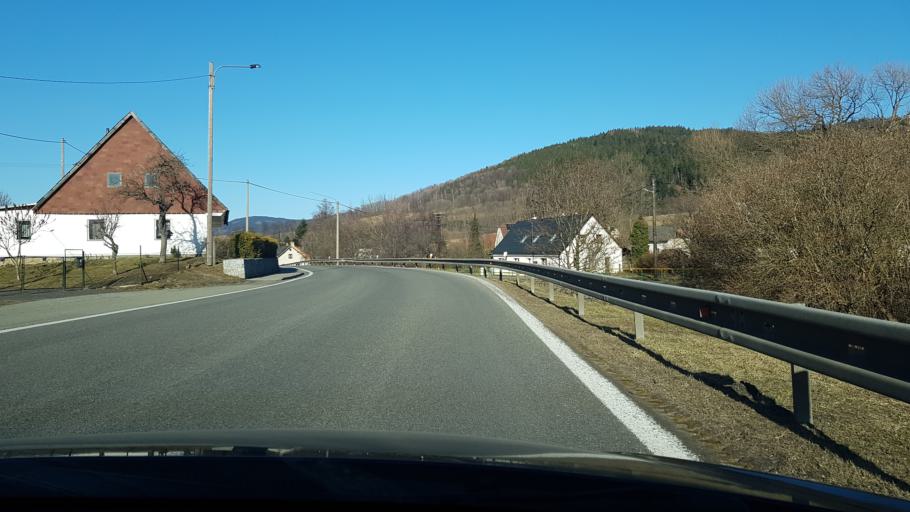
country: CZ
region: Olomoucky
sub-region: Okres Jesenik
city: Jesenik
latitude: 50.1751
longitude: 17.1974
